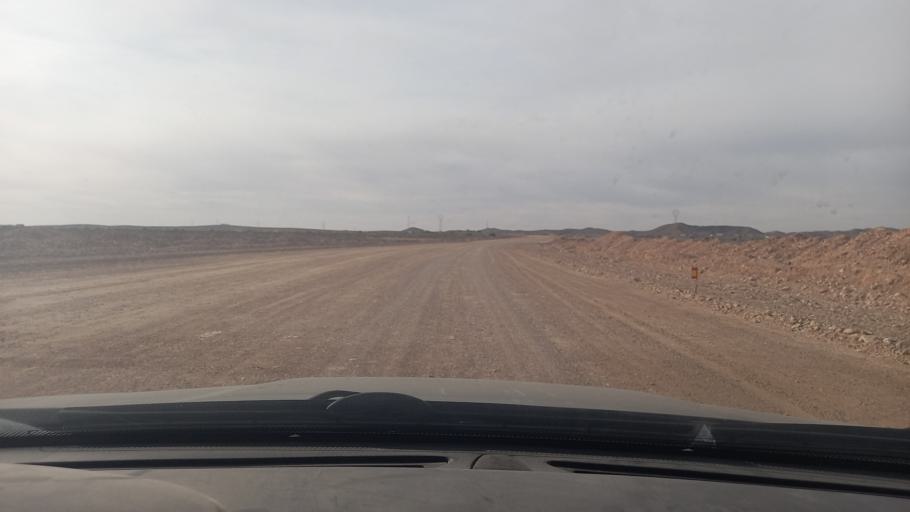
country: TN
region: Tataouine
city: Tataouine
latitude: 33.1353
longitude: 10.5044
